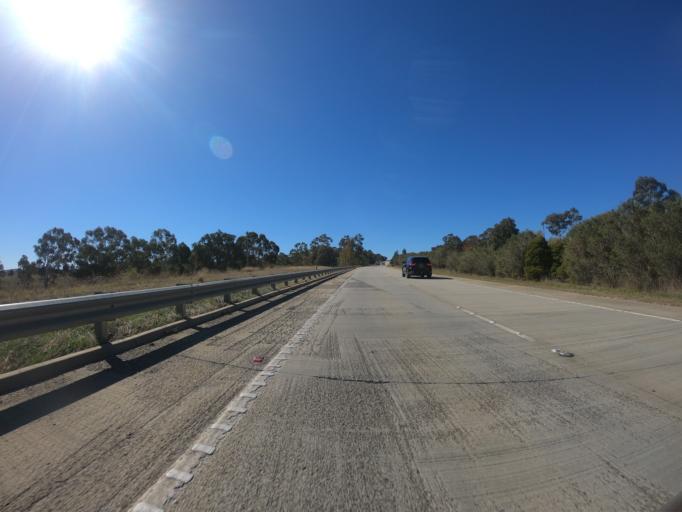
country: AU
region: New South Wales
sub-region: Yass Valley
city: Gundaroo
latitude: -35.1171
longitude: 149.3516
